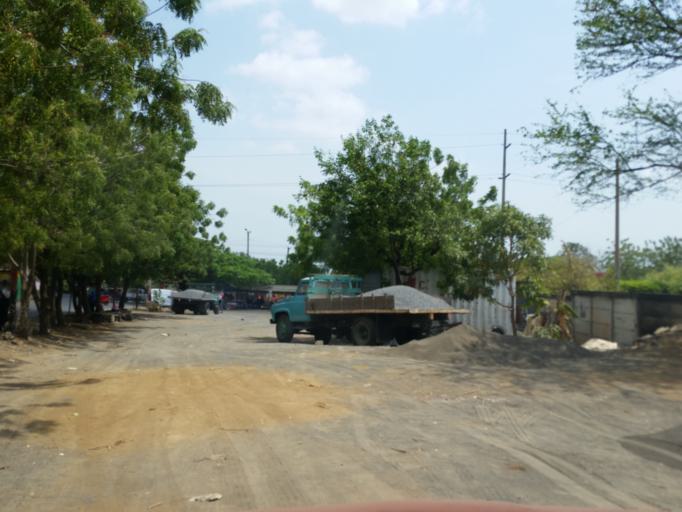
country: NI
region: Managua
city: Managua
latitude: 12.1251
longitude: -86.2886
